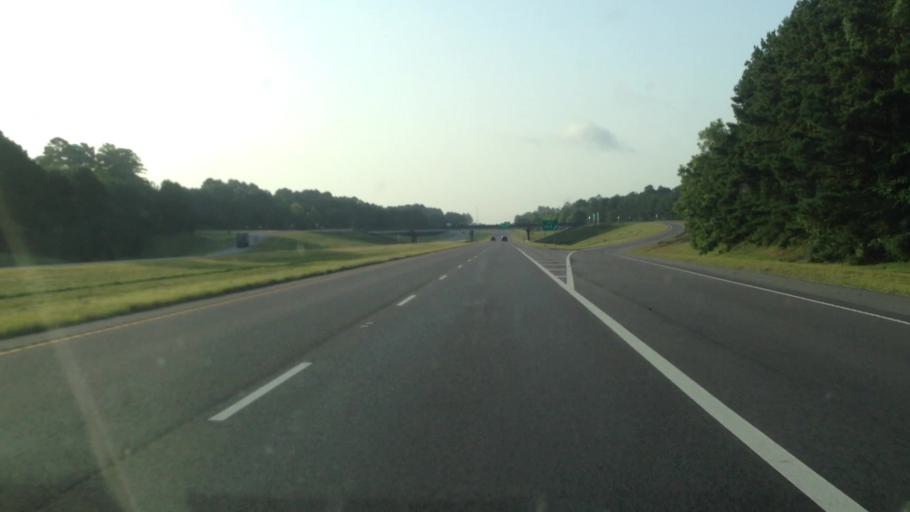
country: US
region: Louisiana
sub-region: Rapides Parish
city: Boyce
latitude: 31.4120
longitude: -92.7208
